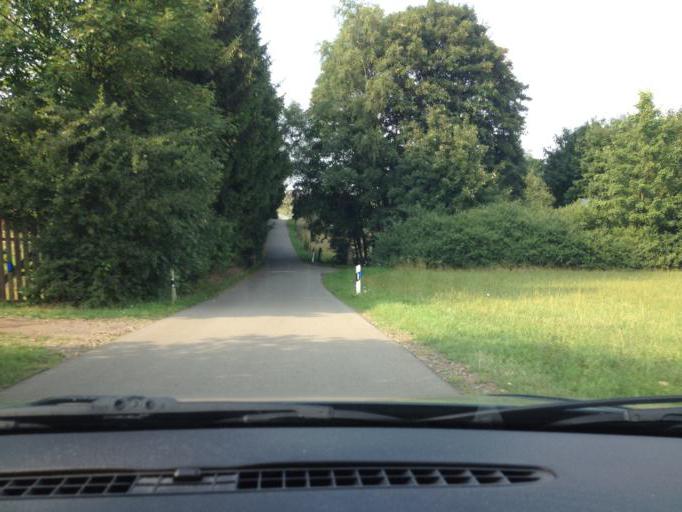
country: DE
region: Saarland
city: Namborn
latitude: 49.5284
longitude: 7.1416
